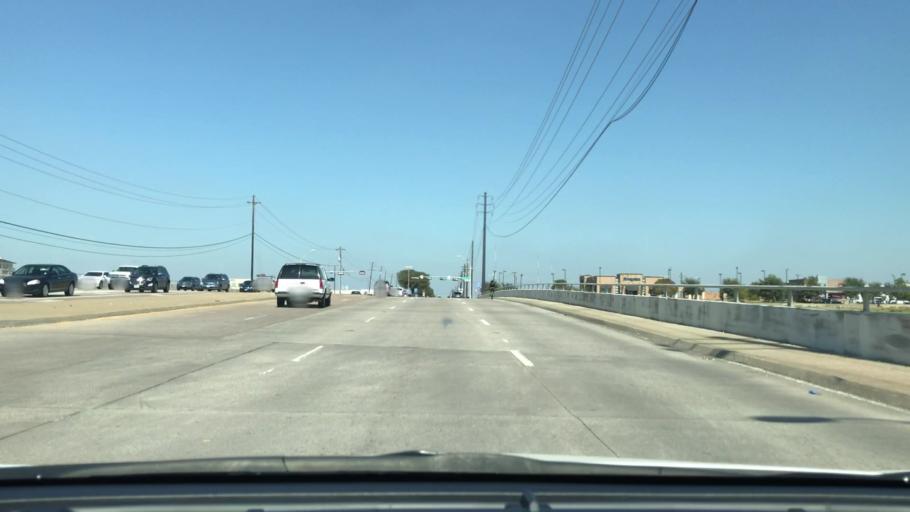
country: US
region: Texas
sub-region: Dallas County
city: Coppell
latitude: 32.9227
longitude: -96.9936
